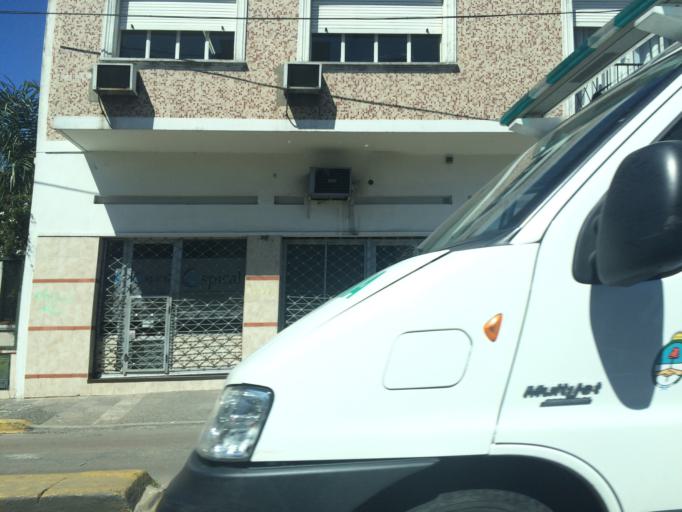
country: AR
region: Buenos Aires
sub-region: Partido de Lomas de Zamora
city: Lomas de Zamora
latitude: -34.7356
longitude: -58.3958
